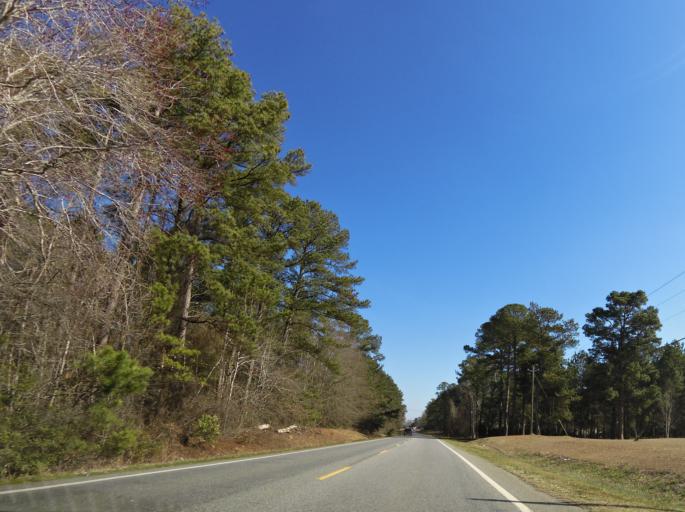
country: US
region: Georgia
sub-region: Bleckley County
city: Cochran
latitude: 32.3696
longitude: -83.3744
